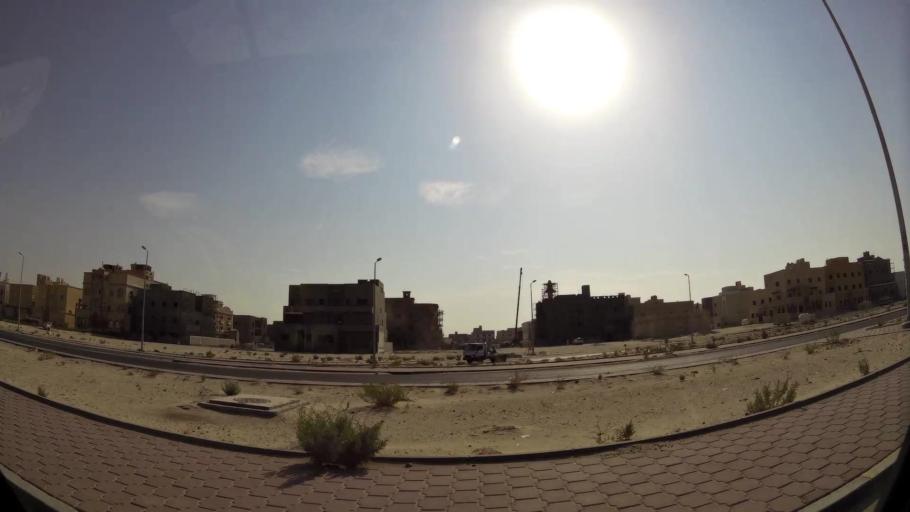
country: KW
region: Al Ahmadi
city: Al Wafrah
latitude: 28.7882
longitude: 48.0361
